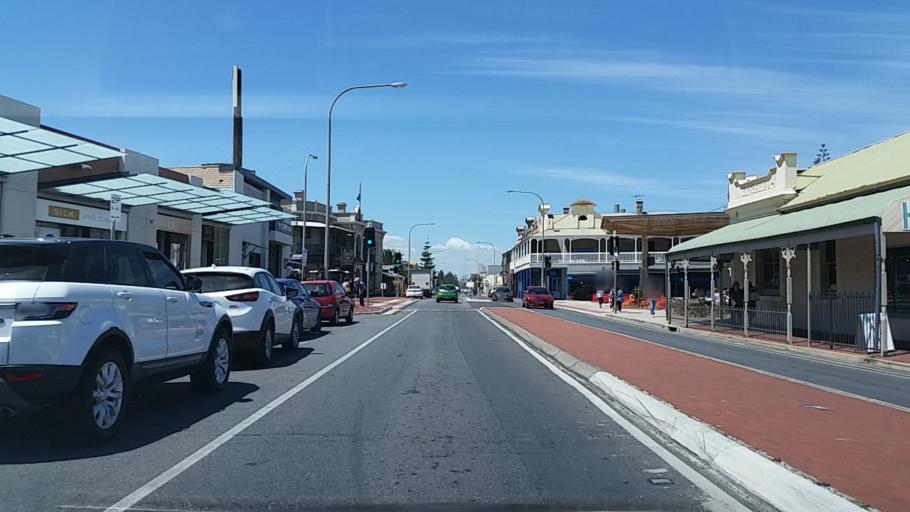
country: AU
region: South Australia
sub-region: Charles Sturt
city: Henley Beach
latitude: -34.9191
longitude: 138.4942
